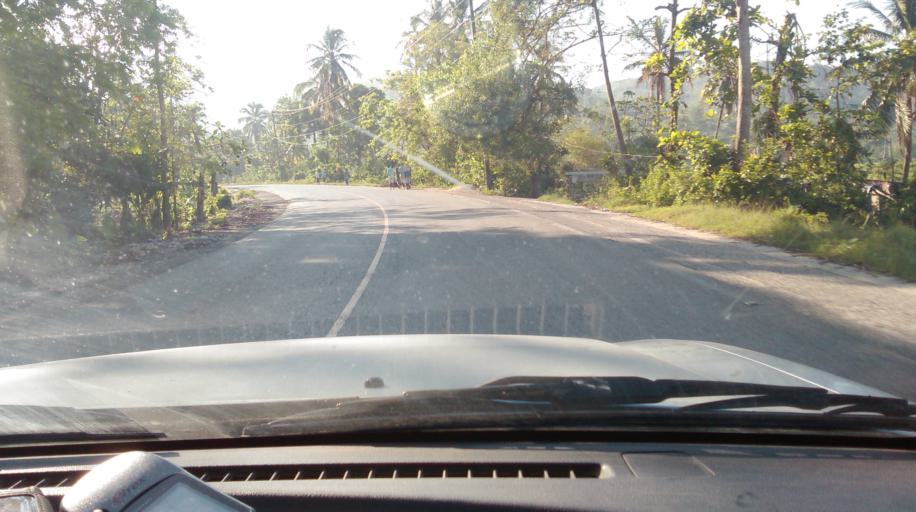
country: HT
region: Grandans
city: Petite Riviere de Nippes
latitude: 18.3470
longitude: -73.2618
